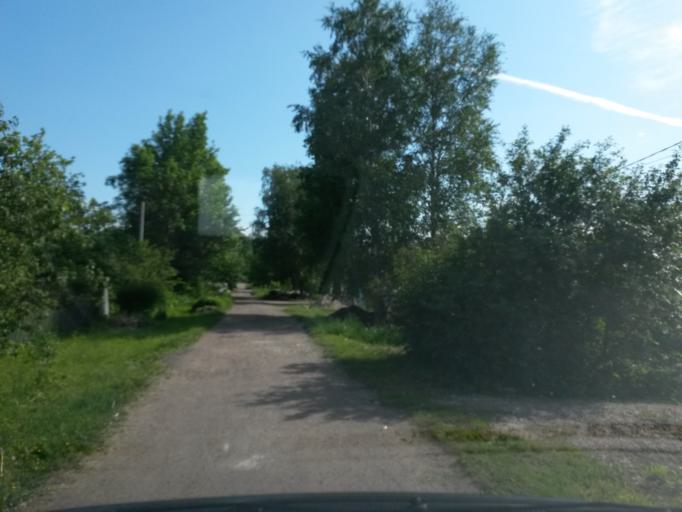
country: RU
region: Jaroslavl
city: Yaroslavl
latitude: 57.6436
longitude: 39.7879
